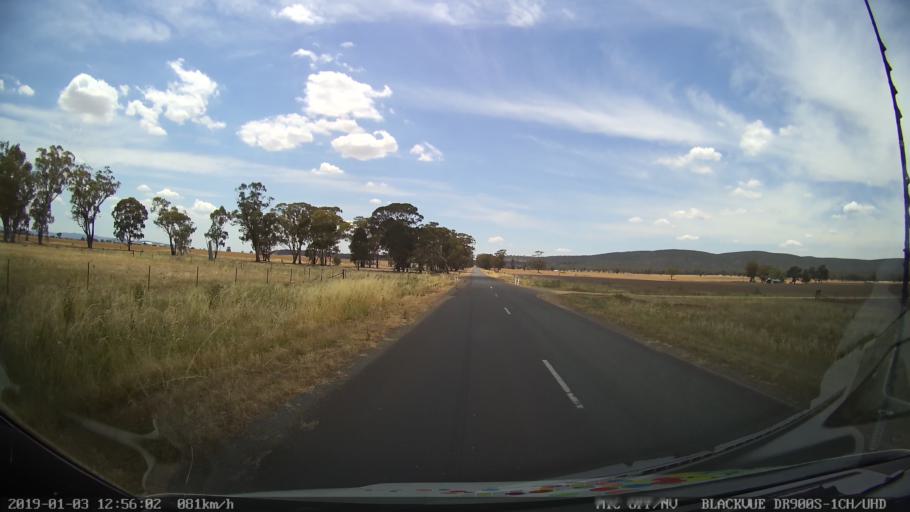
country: AU
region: New South Wales
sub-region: Weddin
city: Grenfell
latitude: -33.6462
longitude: 148.3394
